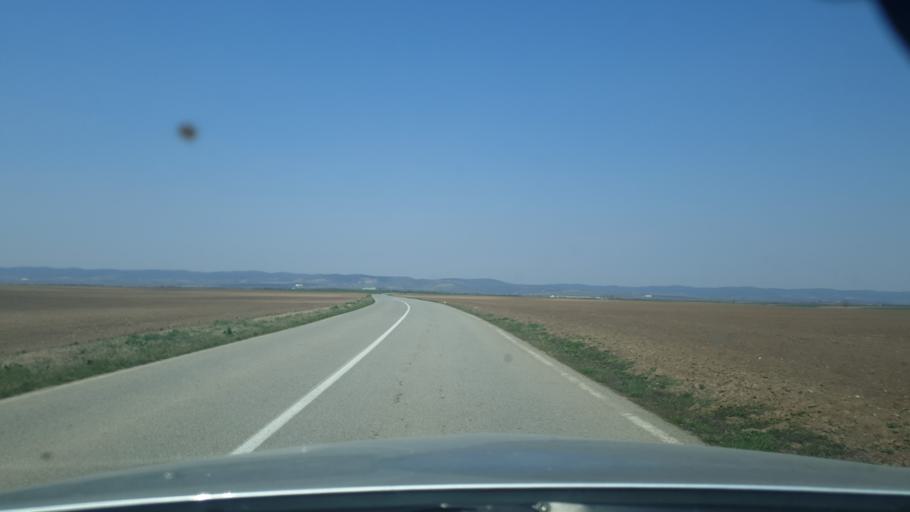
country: RS
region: Autonomna Pokrajina Vojvodina
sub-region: Sremski Okrug
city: Ruma
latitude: 45.0378
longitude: 19.7615
